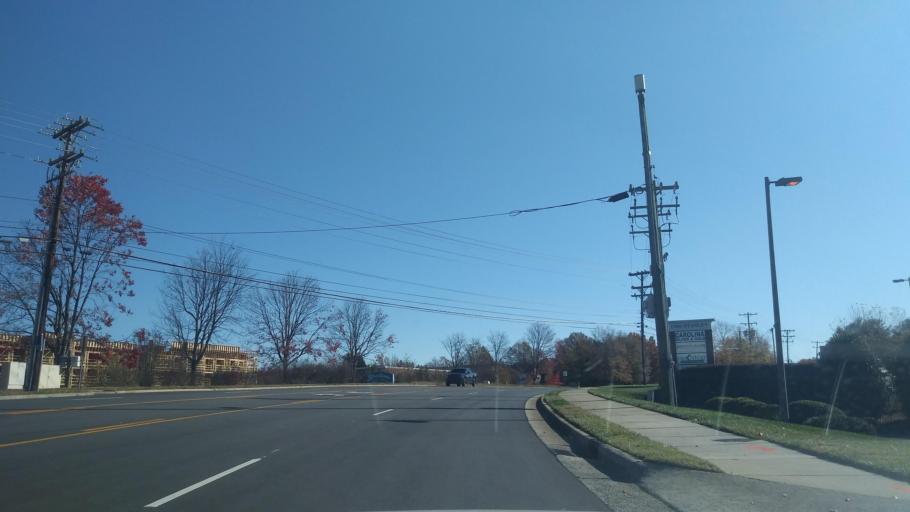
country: US
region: North Carolina
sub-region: Guilford County
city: Jamestown
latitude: 36.0534
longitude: -79.8906
